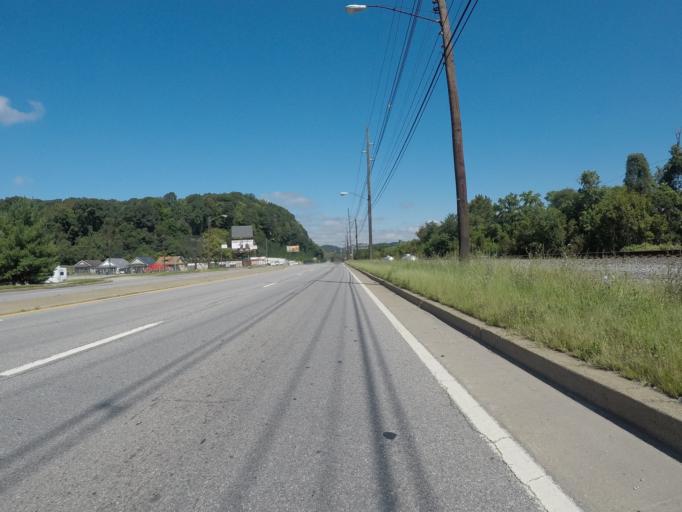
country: US
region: Kentucky
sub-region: Boyd County
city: Ashland
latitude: 38.4543
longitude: -82.6125
